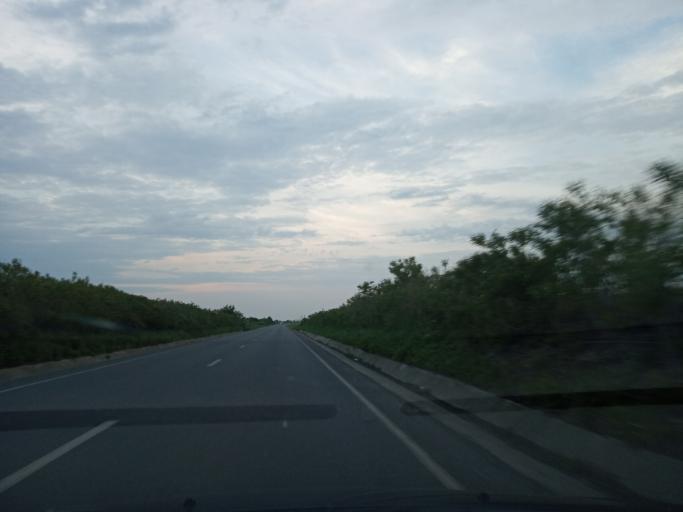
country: RO
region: Timis
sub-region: Comuna Voiteg
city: Voiteg
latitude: 45.4391
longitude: 21.2319
